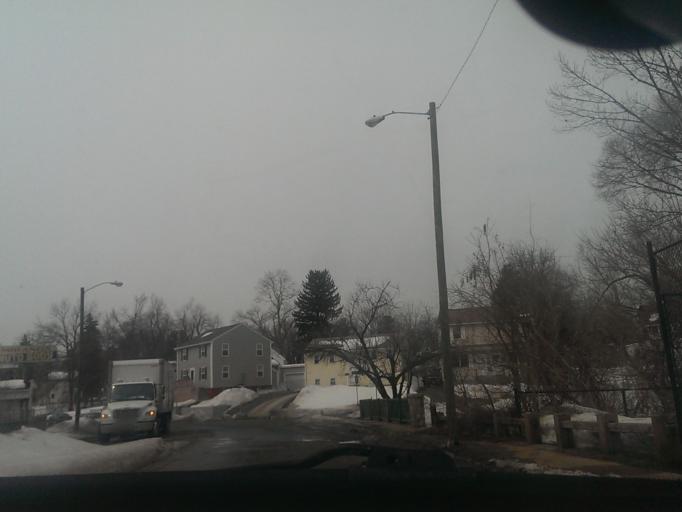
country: US
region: Massachusetts
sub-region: Hampden County
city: Springfield
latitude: 42.0936
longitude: -72.5692
